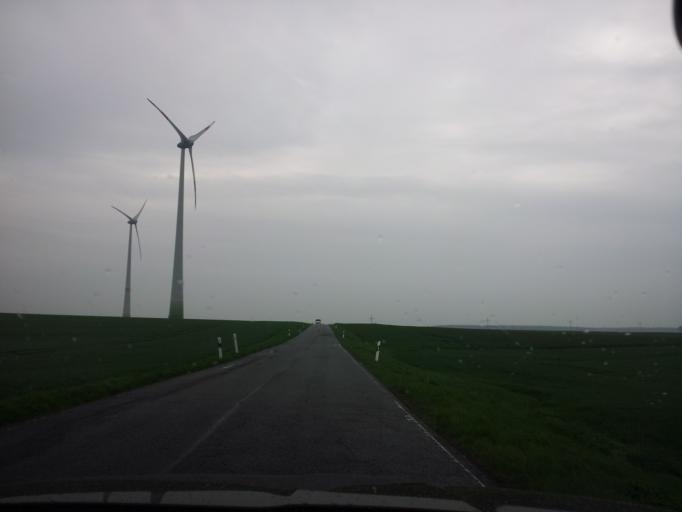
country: DE
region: Saxony-Anhalt
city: Kropstadt
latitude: 51.9863
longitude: 12.8009
